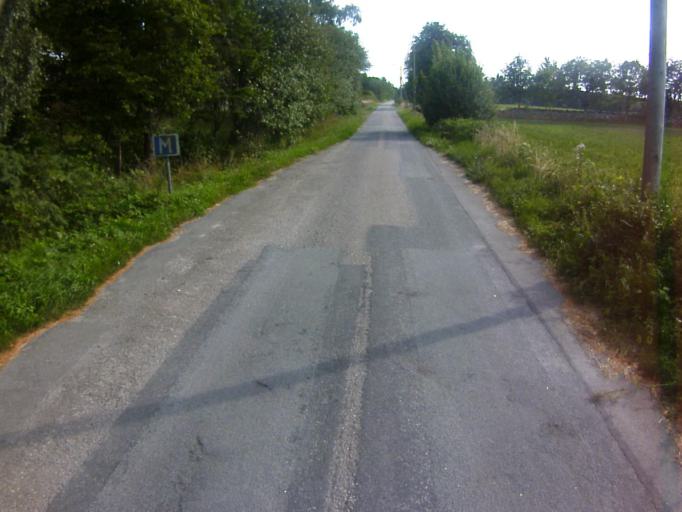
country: SE
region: Blekinge
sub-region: Solvesborgs Kommun
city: Soelvesborg
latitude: 56.0013
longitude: 14.6719
